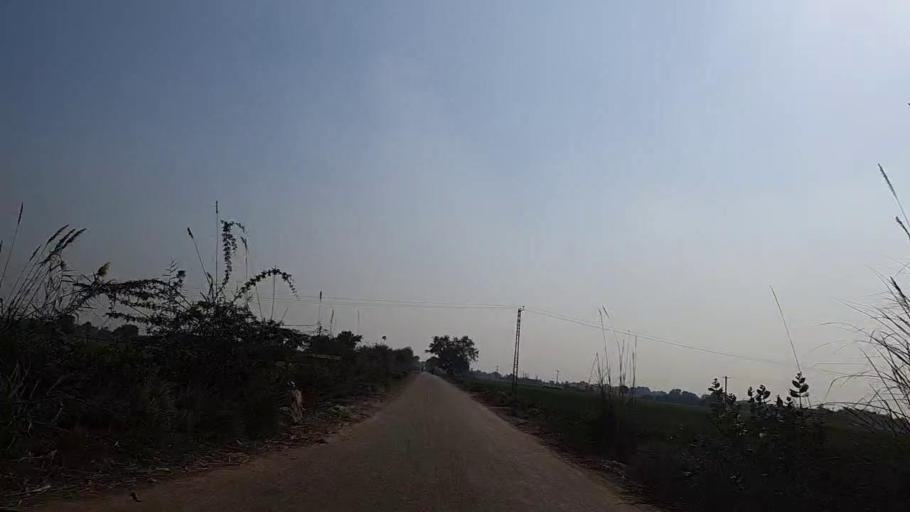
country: PK
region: Sindh
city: Sakrand
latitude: 26.0818
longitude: 68.2900
